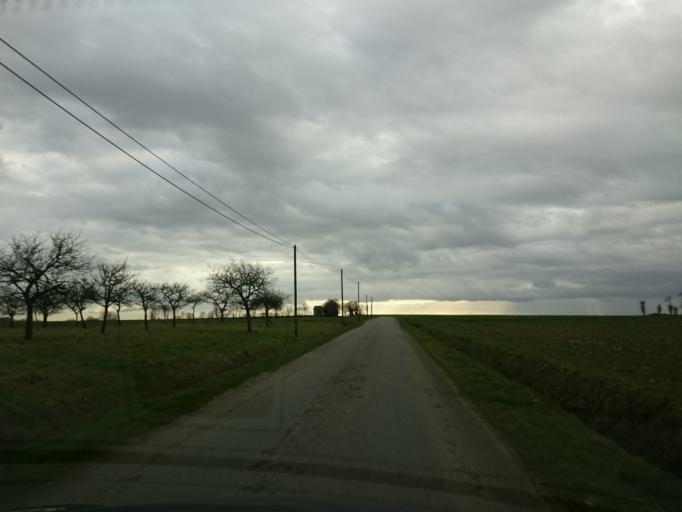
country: FR
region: Brittany
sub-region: Departement d'Ille-et-Vilaine
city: Pance
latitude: 47.9066
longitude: -1.6440
